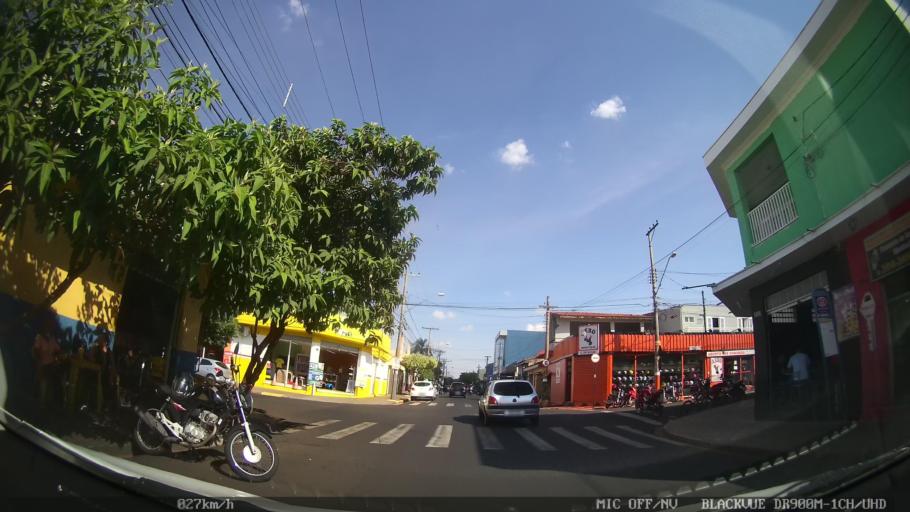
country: BR
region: Sao Paulo
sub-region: Ribeirao Preto
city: Ribeirao Preto
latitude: -21.1870
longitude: -47.8273
